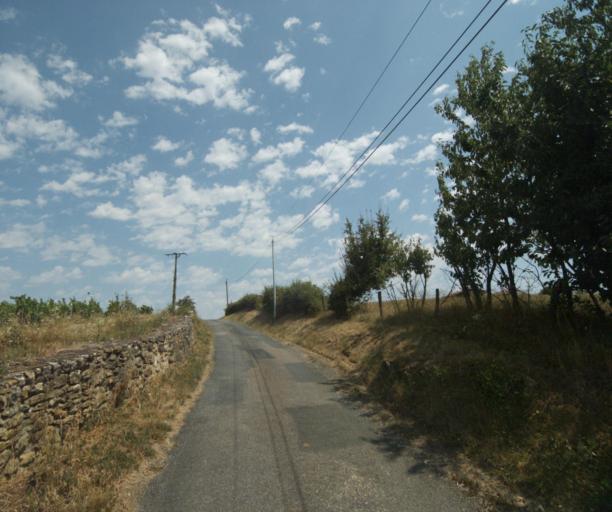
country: FR
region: Rhone-Alpes
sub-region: Departement du Rhone
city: Saint-Germain-Nuelles
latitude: 45.8506
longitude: 4.6257
